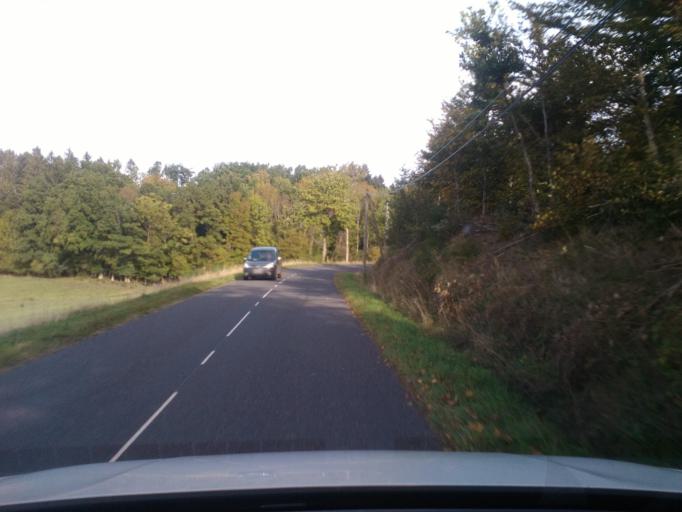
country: FR
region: Lorraine
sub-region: Departement des Vosges
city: Senones
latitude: 48.3599
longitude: 7.0252
